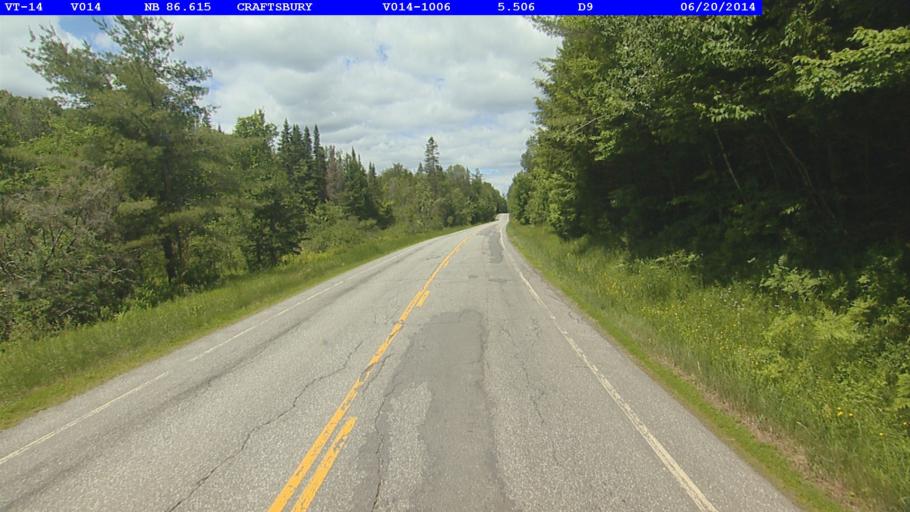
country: US
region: Vermont
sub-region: Caledonia County
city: Hardwick
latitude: 44.6698
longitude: -72.4048
